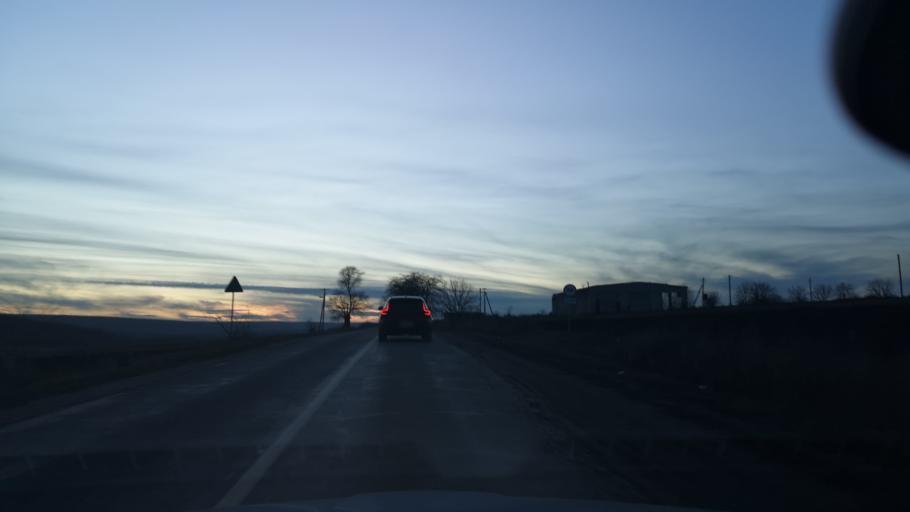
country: MD
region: Orhei
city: Orhei
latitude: 47.2994
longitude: 28.9127
